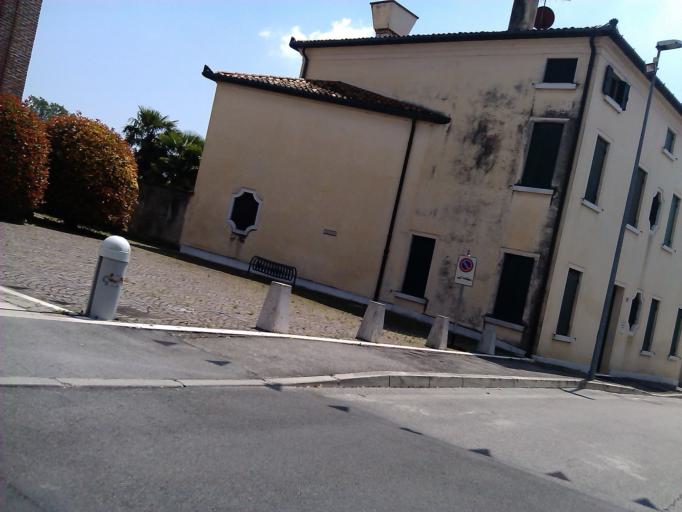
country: IT
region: Veneto
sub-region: Provincia di Venezia
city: Fiesso
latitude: 45.4120
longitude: 12.0525
